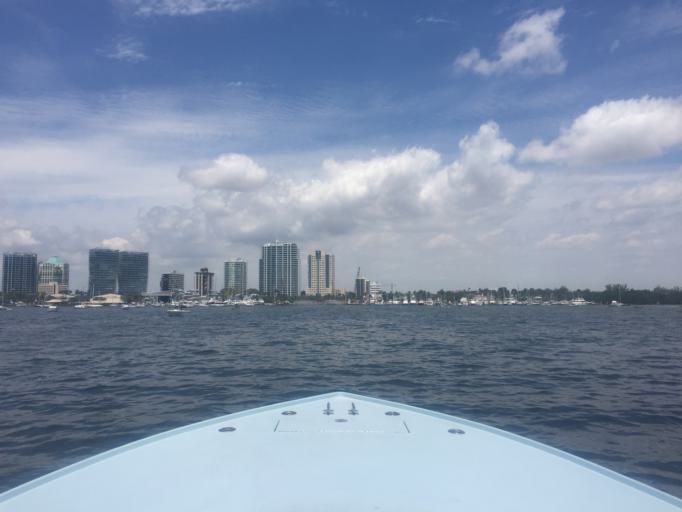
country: US
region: Florida
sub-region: Miami-Dade County
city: Coconut Grove
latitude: 25.7273
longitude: -80.2265
